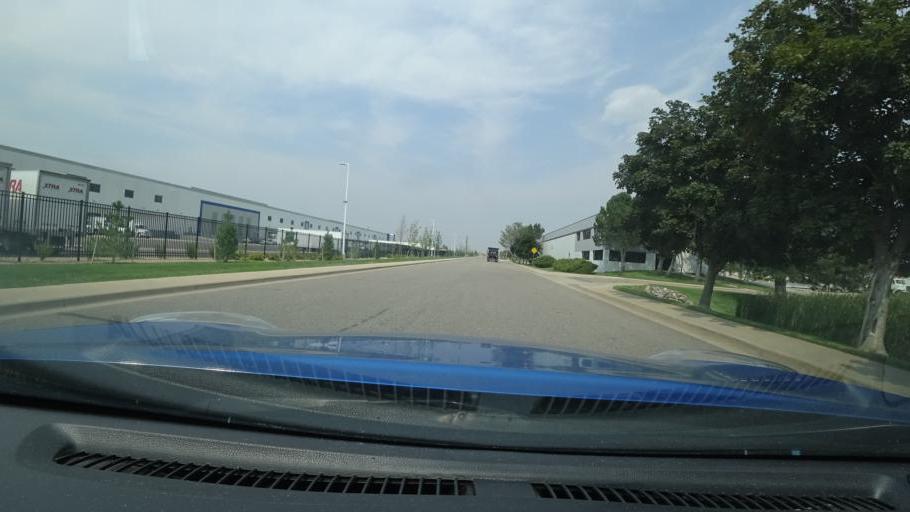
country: US
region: Colorado
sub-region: Adams County
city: Aurora
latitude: 39.7653
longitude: -104.7425
